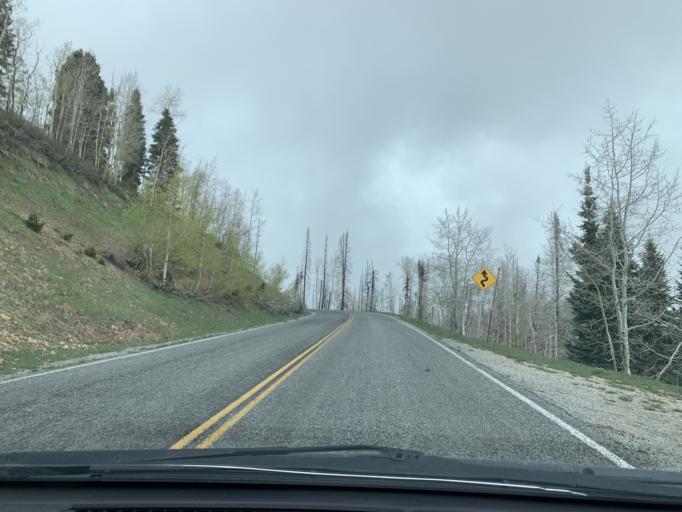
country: US
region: Utah
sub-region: Utah County
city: Elk Ridge
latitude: 39.8844
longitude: -111.6875
